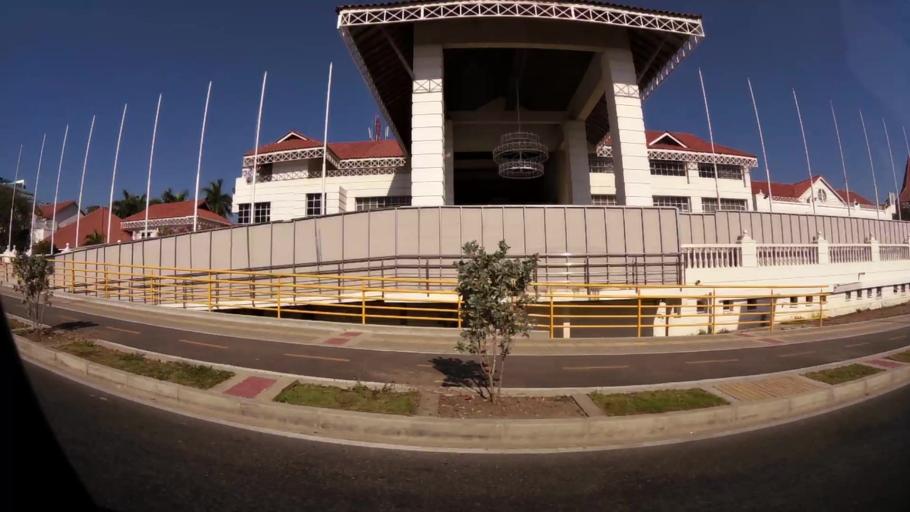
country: CO
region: Bolivar
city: Cartagena
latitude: 10.4599
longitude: -75.5061
